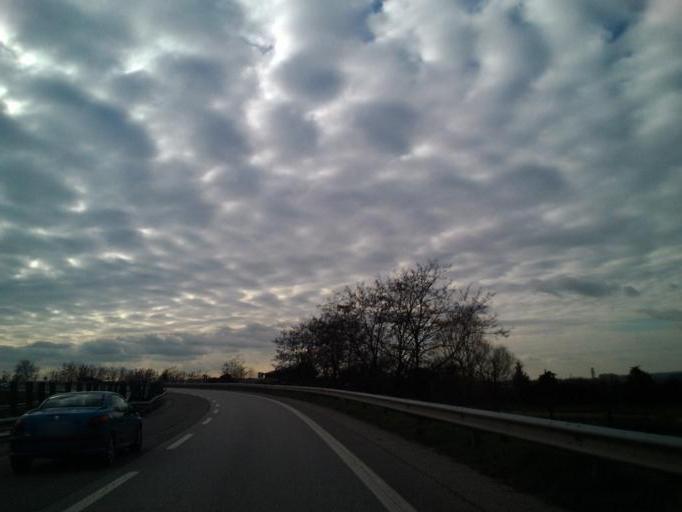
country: IT
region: Veneto
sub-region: Provincia di Verona
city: San Martino Buon Albergo
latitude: 45.4166
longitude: 11.1089
